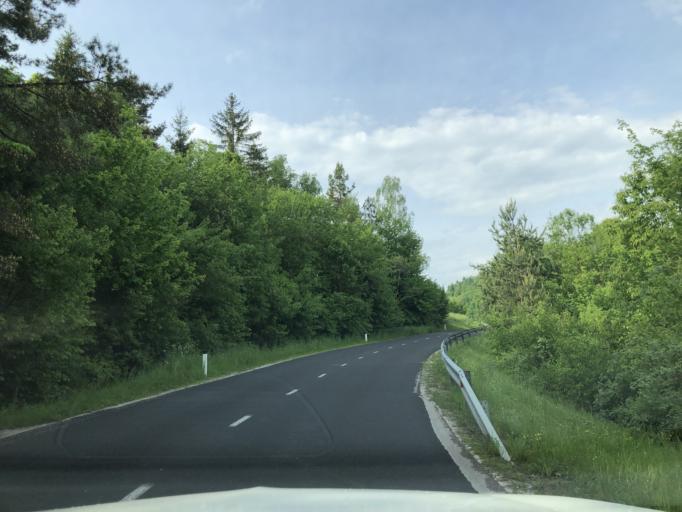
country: SI
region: Velike Lasce
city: Velike Lasce
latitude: 45.8163
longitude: 14.6270
